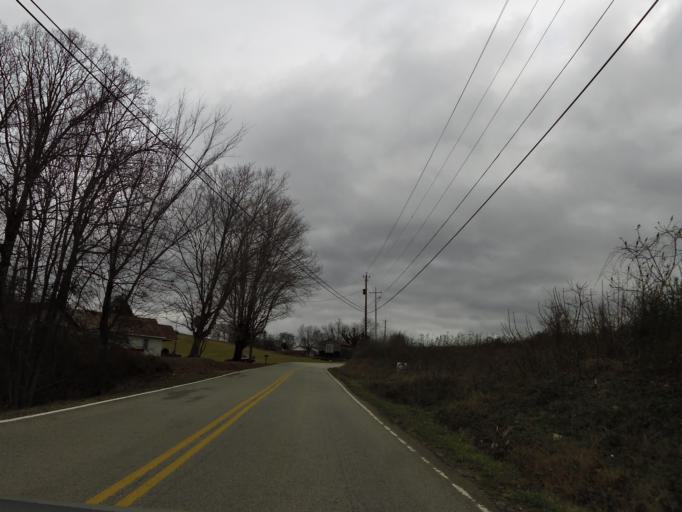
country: US
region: Tennessee
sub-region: Grainger County
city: Blaine
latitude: 36.1437
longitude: -83.6532
